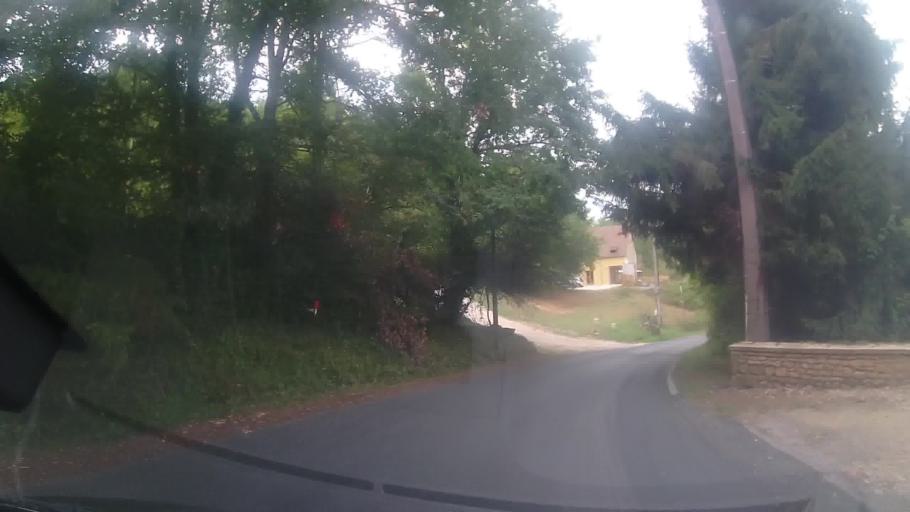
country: FR
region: Aquitaine
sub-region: Departement de la Dordogne
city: Eyvigues-et-Eybenes
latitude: 44.8462
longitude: 1.3653
